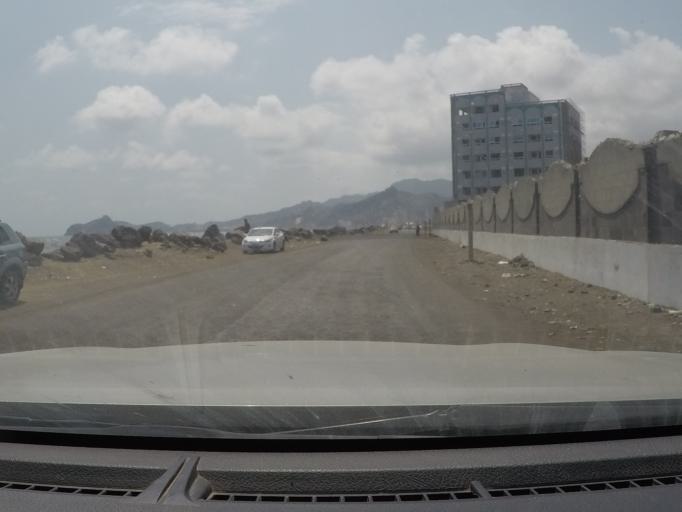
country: YE
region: Aden
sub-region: Khur Maksar
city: Khawr Maksar
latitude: 12.8116
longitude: 45.0437
